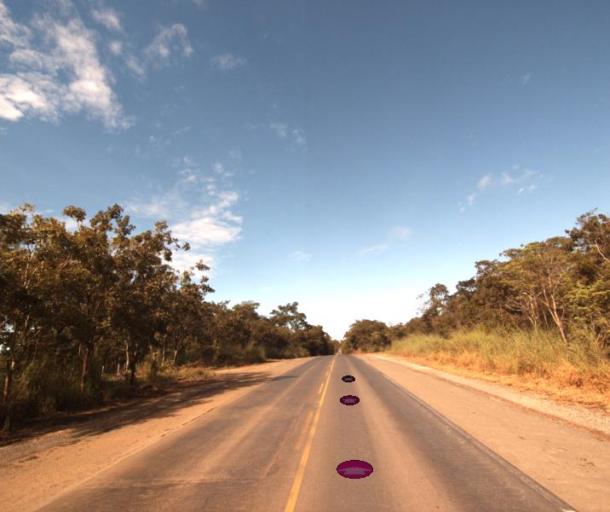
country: BR
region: Goias
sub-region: Itapaci
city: Itapaci
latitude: -14.8131
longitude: -49.2930
